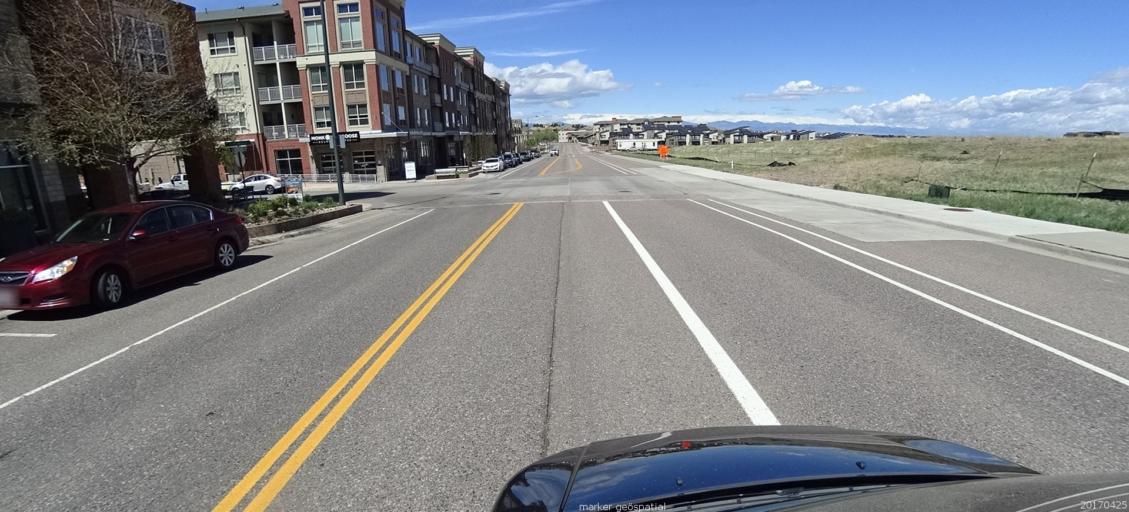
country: US
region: Colorado
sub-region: Adams County
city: Lone Tree
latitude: 39.5303
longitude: -104.8769
